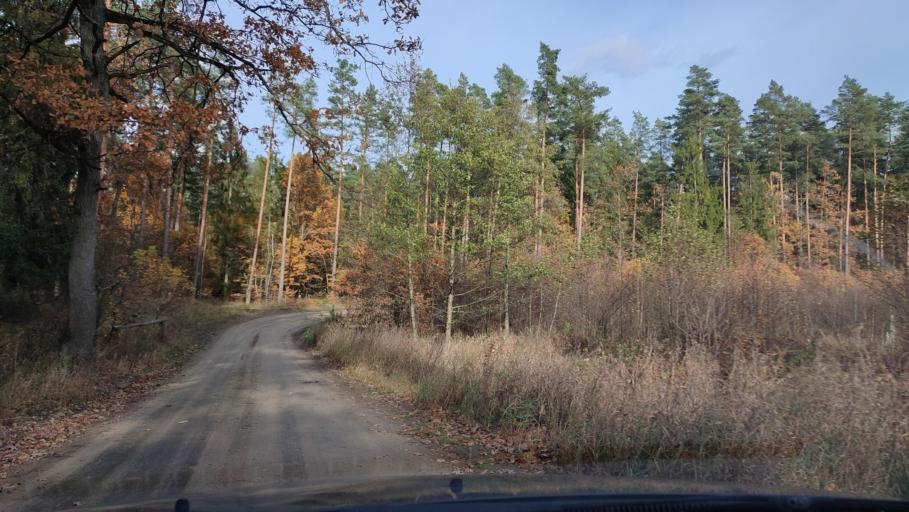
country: PL
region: Warmian-Masurian Voivodeship
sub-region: Powiat szczycienski
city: Szczytno
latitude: 53.5253
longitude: 20.9076
